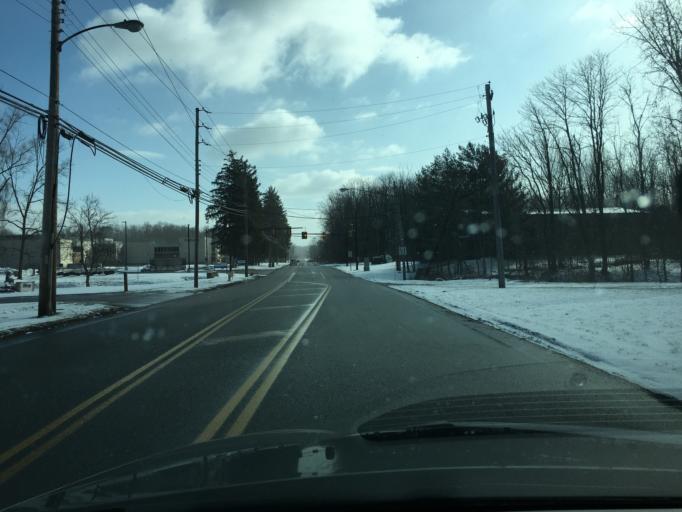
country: US
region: Ohio
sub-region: Summit County
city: Fairlawn
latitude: 41.0998
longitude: -81.5825
